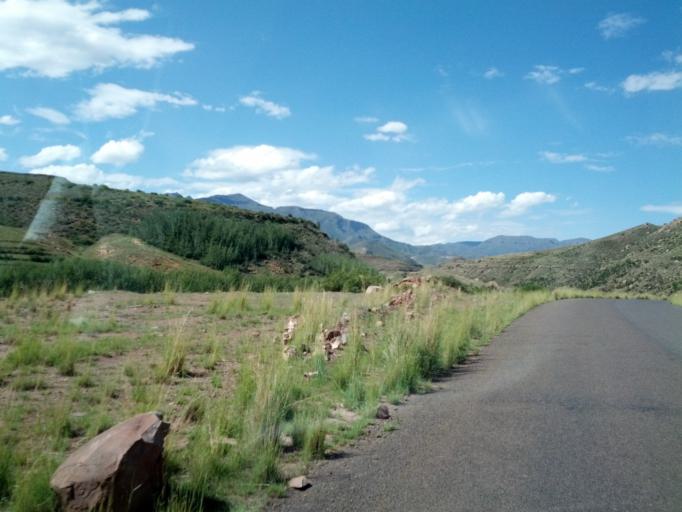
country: LS
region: Qacha's Nek
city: Qacha's Nek
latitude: -30.0756
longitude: 28.4521
